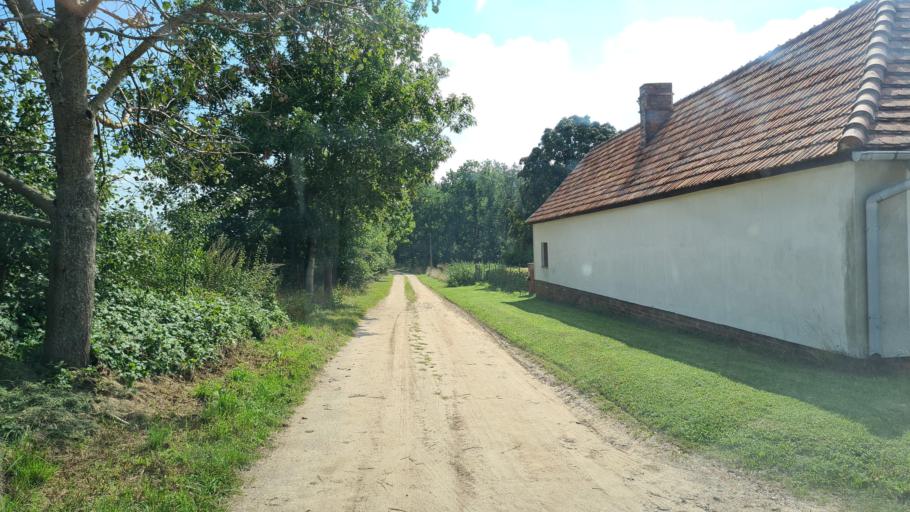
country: DE
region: Brandenburg
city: Sonnewalde
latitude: 51.7302
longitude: 13.6477
